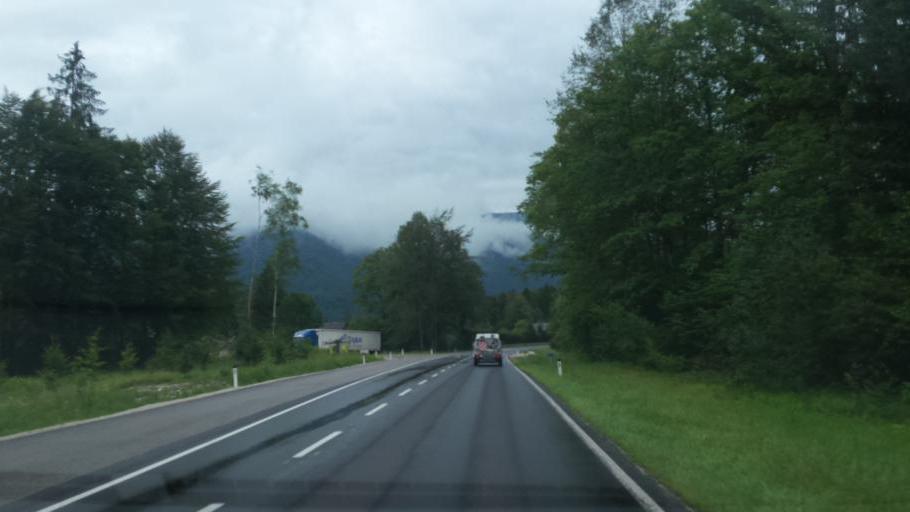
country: AT
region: Upper Austria
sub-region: Politischer Bezirk Gmunden
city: Bad Ischl
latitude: 47.7144
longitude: 13.5629
